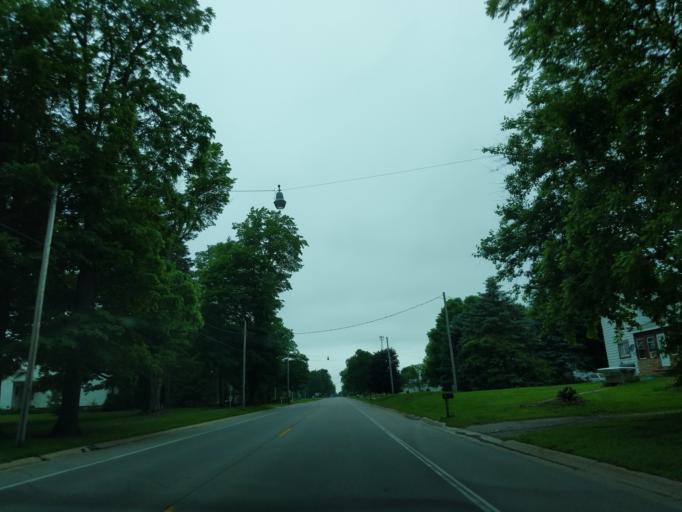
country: US
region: Michigan
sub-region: Hillsdale County
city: Litchfield
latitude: 41.9561
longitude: -84.7739
